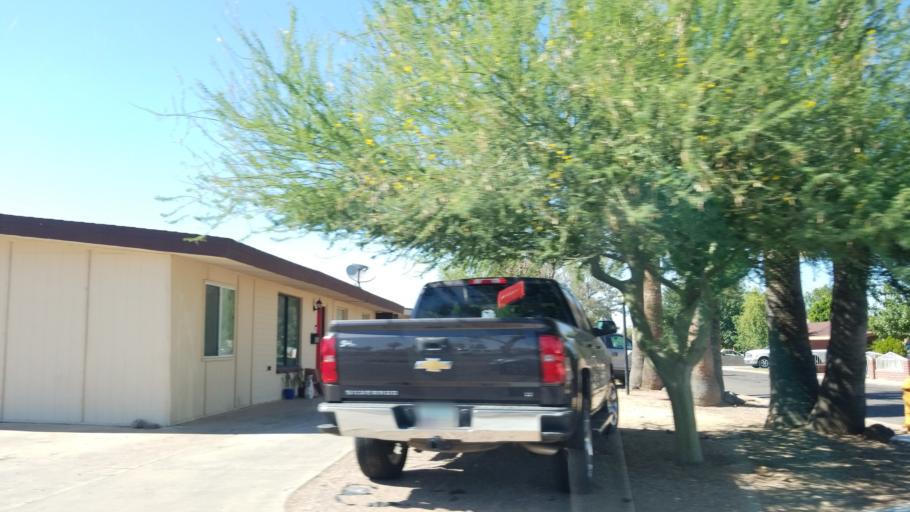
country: US
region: Arizona
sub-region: Maricopa County
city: Glendale
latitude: 33.5241
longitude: -112.1283
